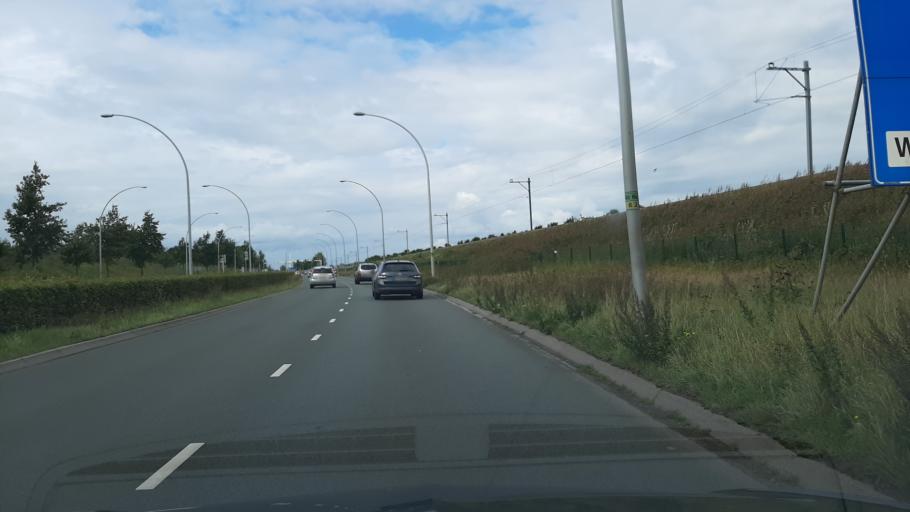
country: NL
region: Overijssel
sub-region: Gemeente Zwolle
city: Zwolle
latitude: 52.5224
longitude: 6.0593
